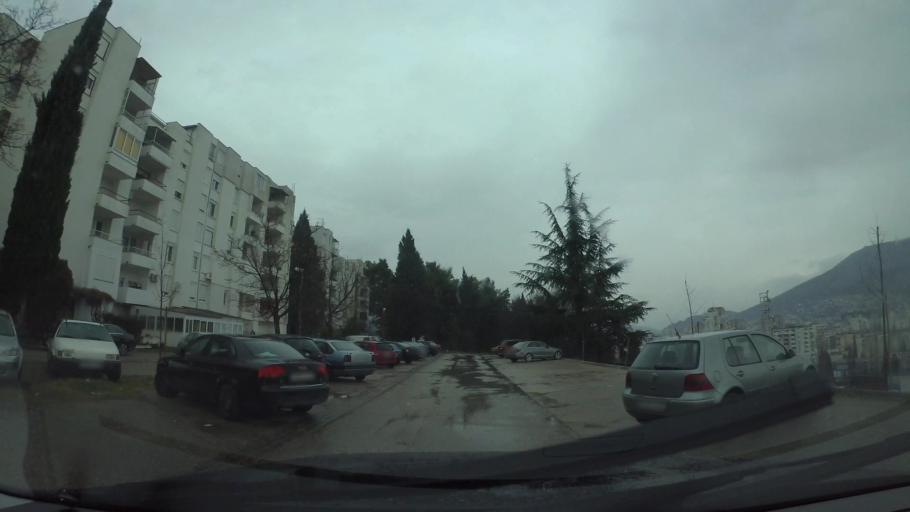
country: BA
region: Federation of Bosnia and Herzegovina
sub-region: Hercegovacko-Bosanski Kanton
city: Mostar
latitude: 43.3460
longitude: 17.7938
